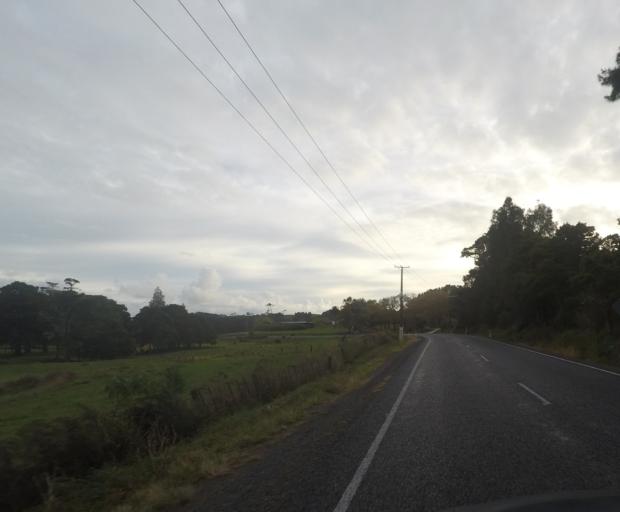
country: NZ
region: Auckland
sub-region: Auckland
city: Wellsford
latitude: -36.2157
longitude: 174.5868
